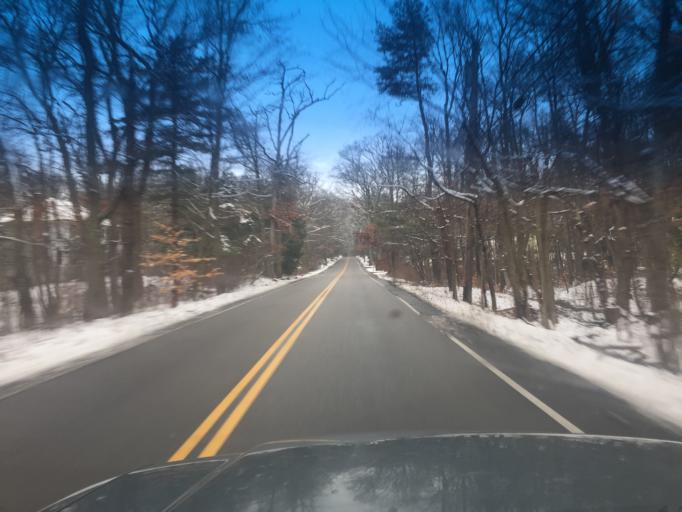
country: US
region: Massachusetts
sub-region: Norfolk County
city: Millis
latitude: 42.1912
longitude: -71.3779
